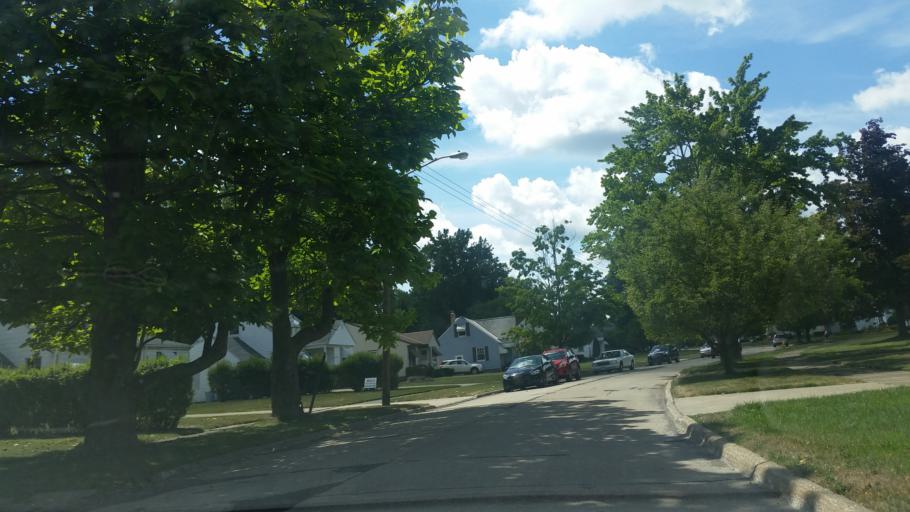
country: US
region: Ohio
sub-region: Cuyahoga County
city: Parma Heights
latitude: 41.3709
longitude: -81.7776
